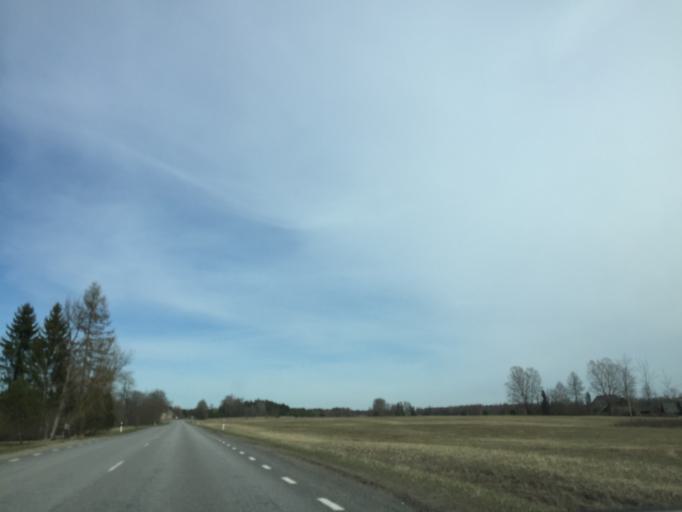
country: EE
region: Vorumaa
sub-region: Antsla vald
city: Vana-Antsla
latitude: 57.9409
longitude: 26.3717
